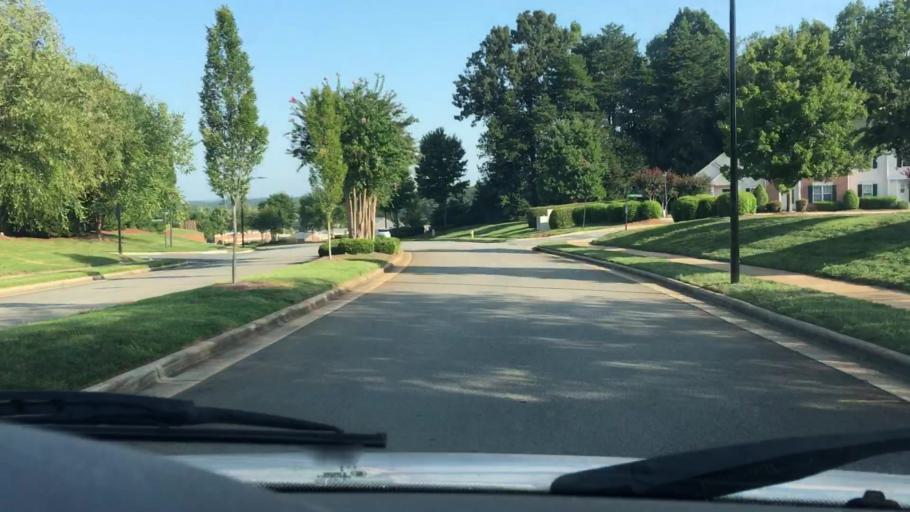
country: US
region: North Carolina
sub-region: Lincoln County
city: Lowesville
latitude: 35.4412
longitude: -80.9948
